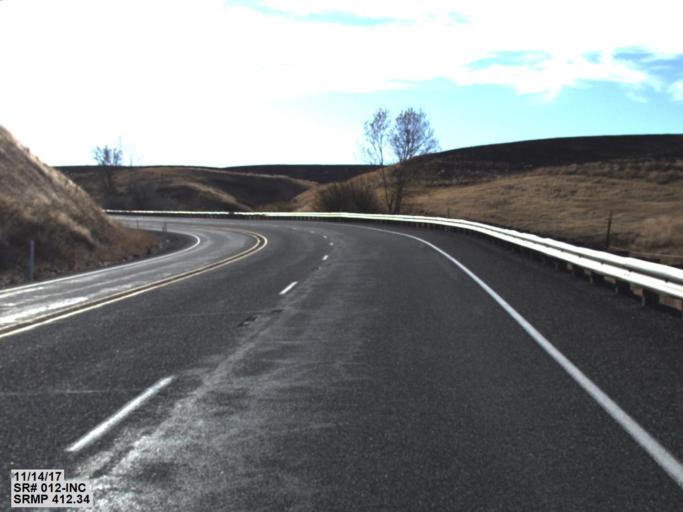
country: US
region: Washington
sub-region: Garfield County
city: Pomeroy
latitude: 46.4427
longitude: -117.4404
